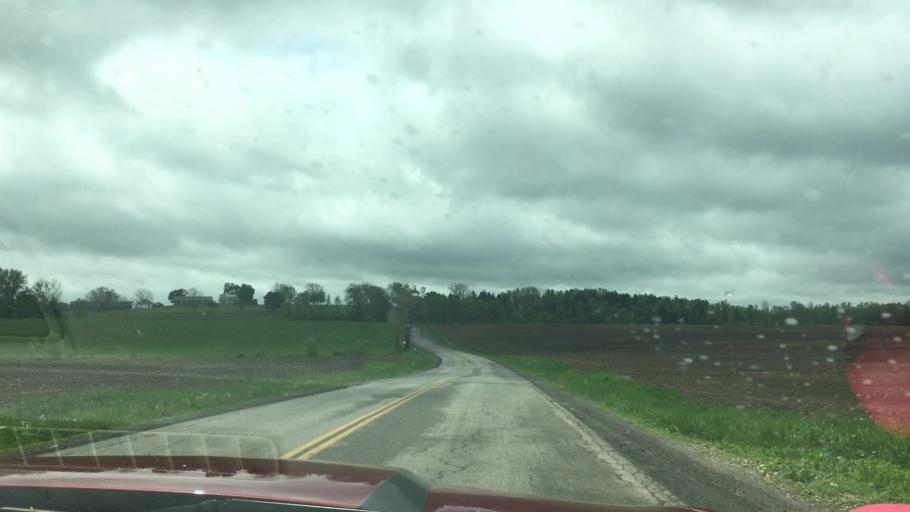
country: US
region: New York
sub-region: Genesee County
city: Batavia
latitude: 43.0903
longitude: -78.1390
